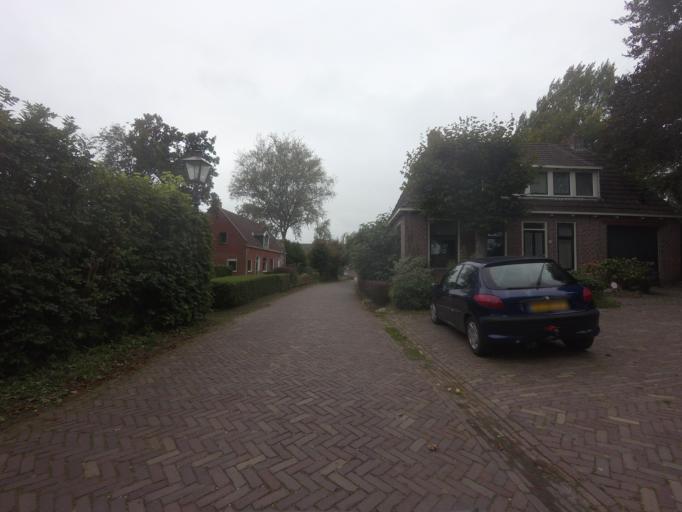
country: NL
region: Friesland
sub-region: Gemeente Leeuwarderadeel
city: Britsum
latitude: 53.2340
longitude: 5.7828
